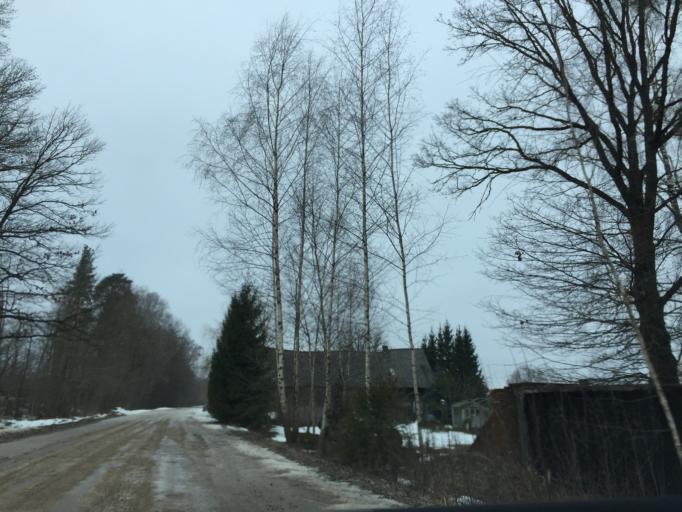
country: LV
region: Ozolnieku
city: Ozolnieki
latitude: 56.6306
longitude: 23.8138
